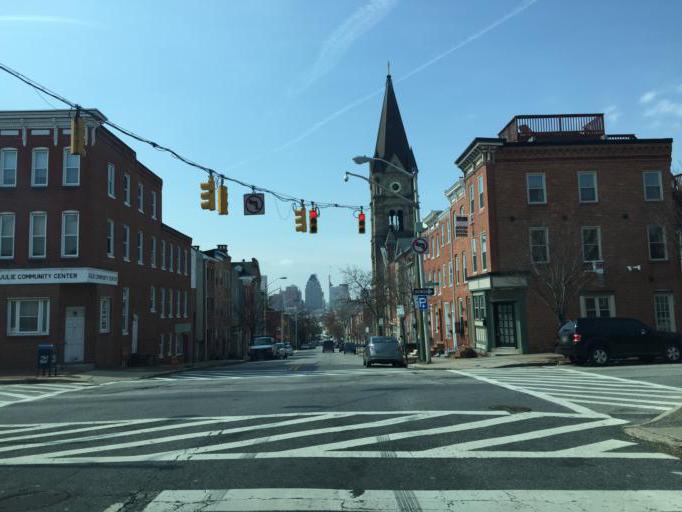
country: US
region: Maryland
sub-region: City of Baltimore
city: Baltimore
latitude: 39.2906
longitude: -76.5889
